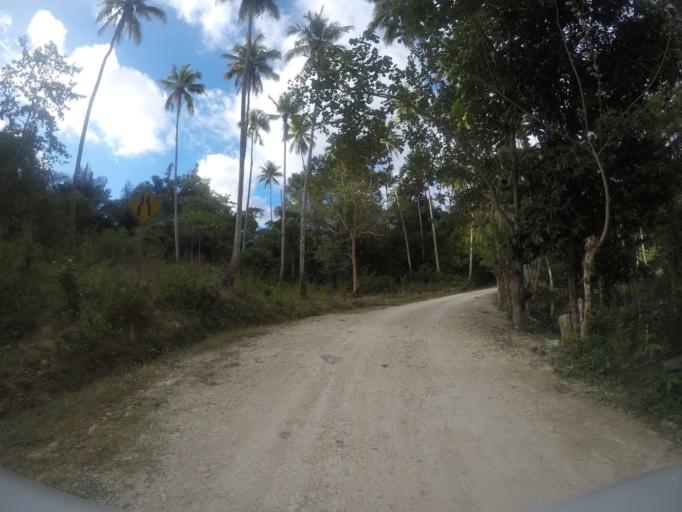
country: TL
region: Lautem
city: Lospalos
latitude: -8.5248
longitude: 126.9377
